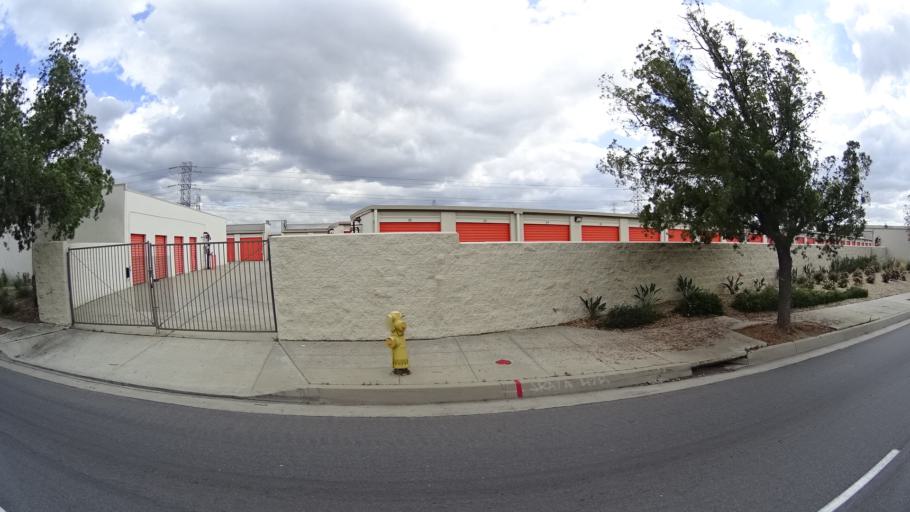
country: US
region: California
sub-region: Los Angeles County
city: Mayflower Village
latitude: 34.0903
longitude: -117.9977
